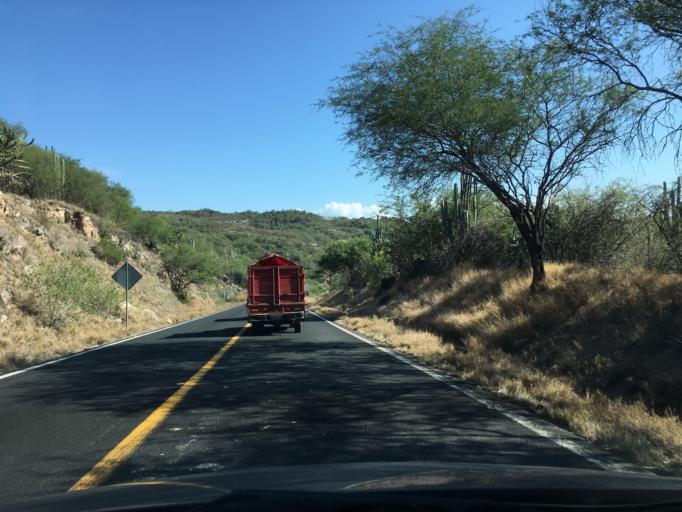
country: MX
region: Hidalgo
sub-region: San Agustin Metzquititlan
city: Mezquititlan
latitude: 20.4582
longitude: -98.6786
